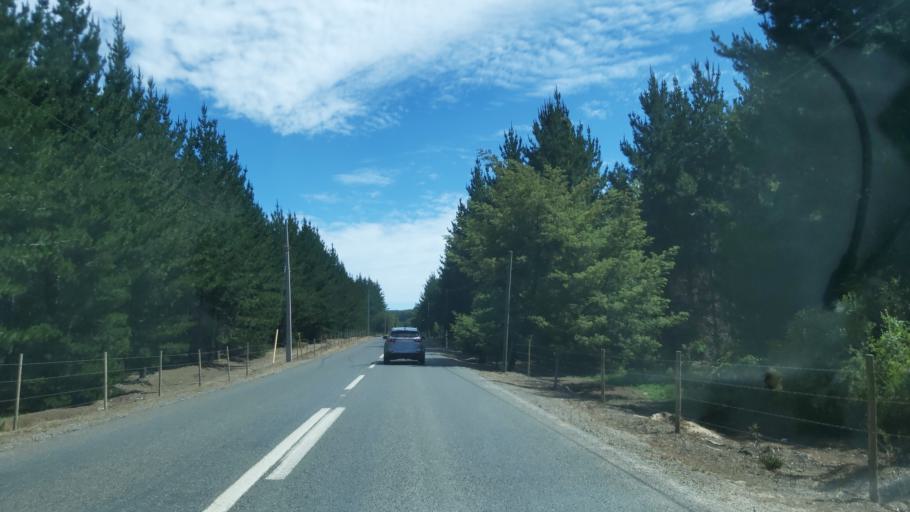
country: CL
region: Maule
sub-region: Provincia de Talca
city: Constitucion
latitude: -35.5295
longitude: -72.5411
